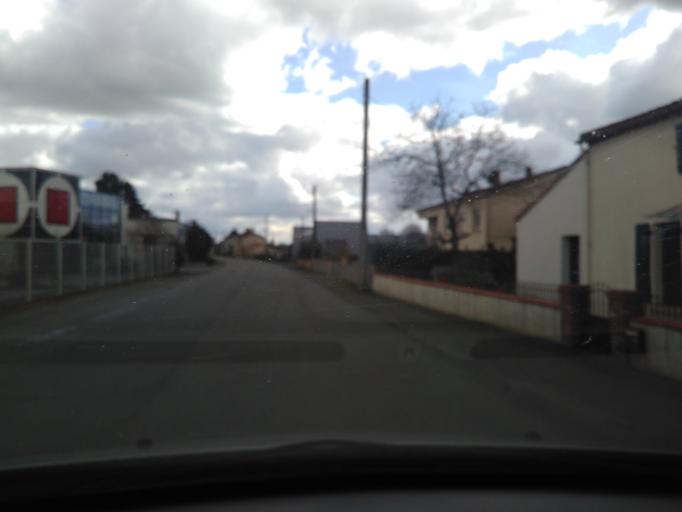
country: FR
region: Pays de la Loire
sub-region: Departement de la Vendee
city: Saint-Martin-des-Noyers
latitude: 46.7299
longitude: -1.1818
